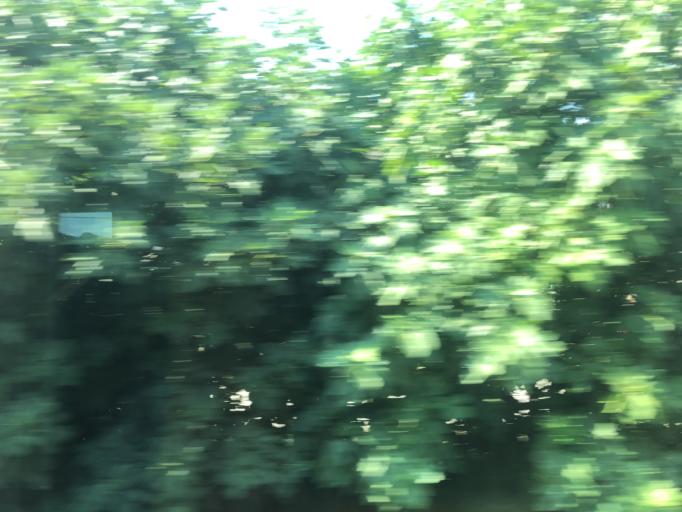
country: IT
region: Emilia-Romagna
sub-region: Forli-Cesena
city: Cesena
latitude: 44.1414
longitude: 12.2622
